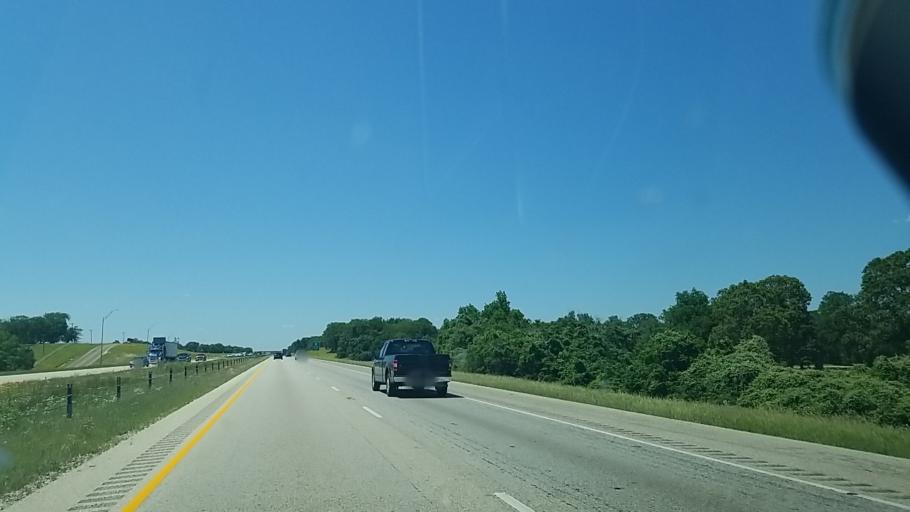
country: US
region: Texas
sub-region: Leon County
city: Buffalo
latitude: 31.4329
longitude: -96.0596
